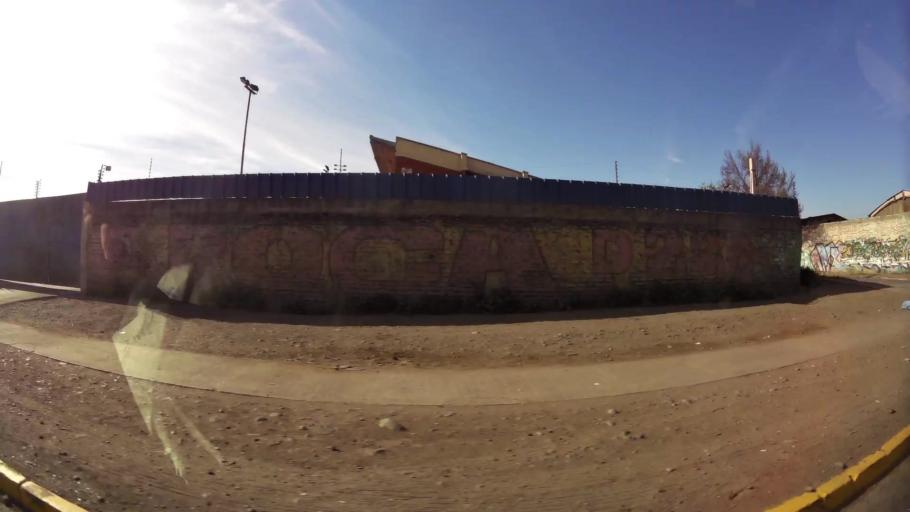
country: CL
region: Santiago Metropolitan
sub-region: Provincia de Santiago
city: Santiago
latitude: -33.4668
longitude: -70.6862
